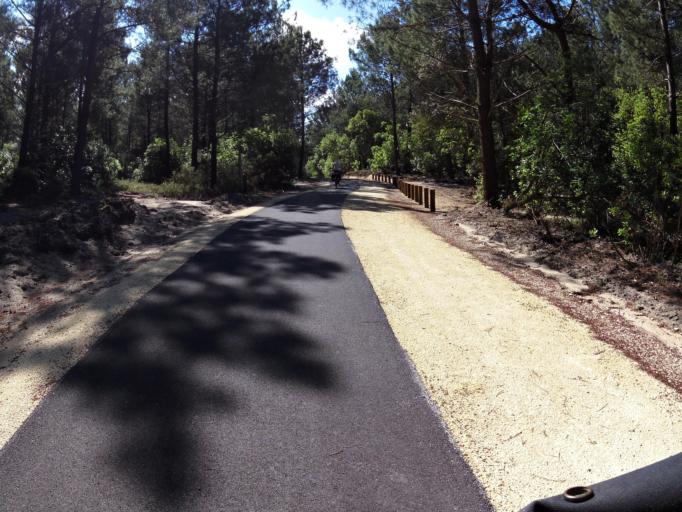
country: FR
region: Aquitaine
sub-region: Departement de la Gironde
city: Lacanau
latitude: 45.0316
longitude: -1.1619
